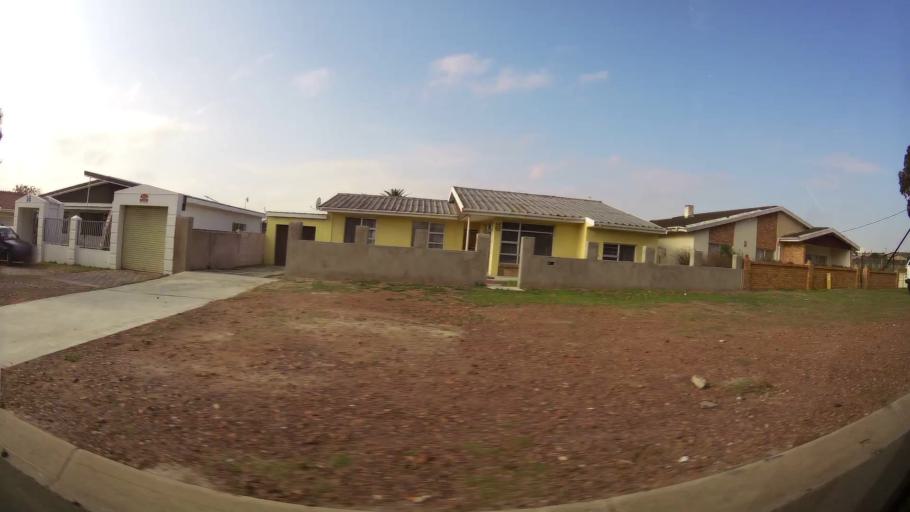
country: ZA
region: Eastern Cape
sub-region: Nelson Mandela Bay Metropolitan Municipality
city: Port Elizabeth
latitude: -33.9171
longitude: 25.5591
